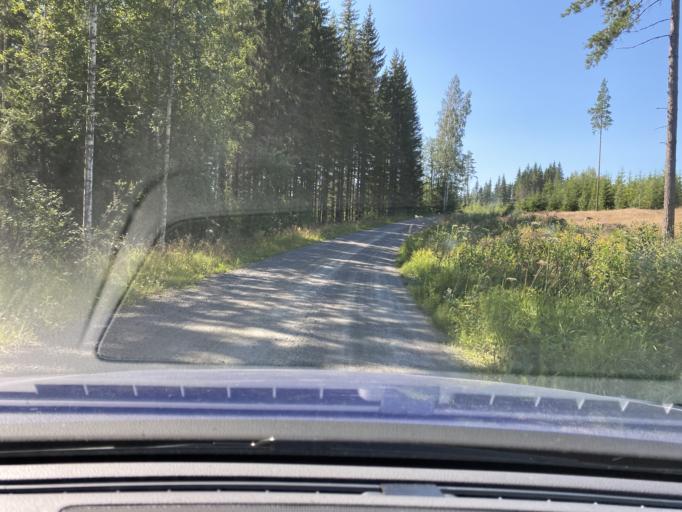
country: FI
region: Central Finland
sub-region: Jaemsae
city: Jaemsae
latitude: 61.8485
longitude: 25.3805
